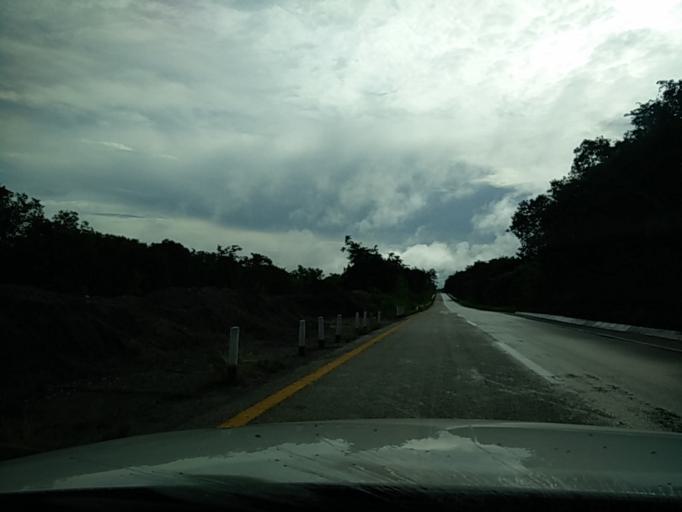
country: MX
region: Yucatan
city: Tunkas
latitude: 20.7638
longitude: -88.7931
